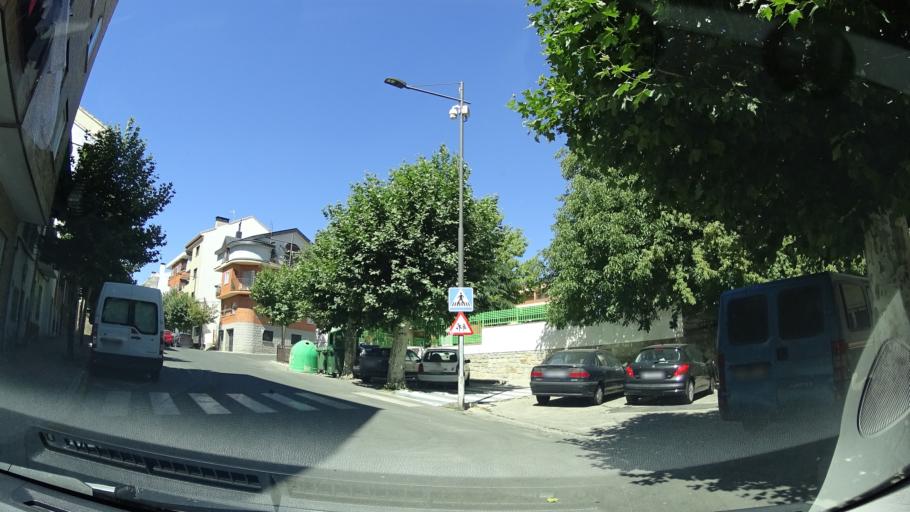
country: ES
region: Castille and Leon
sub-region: Provincia de Avila
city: Las Navas del Marques
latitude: 40.6036
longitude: -4.3315
